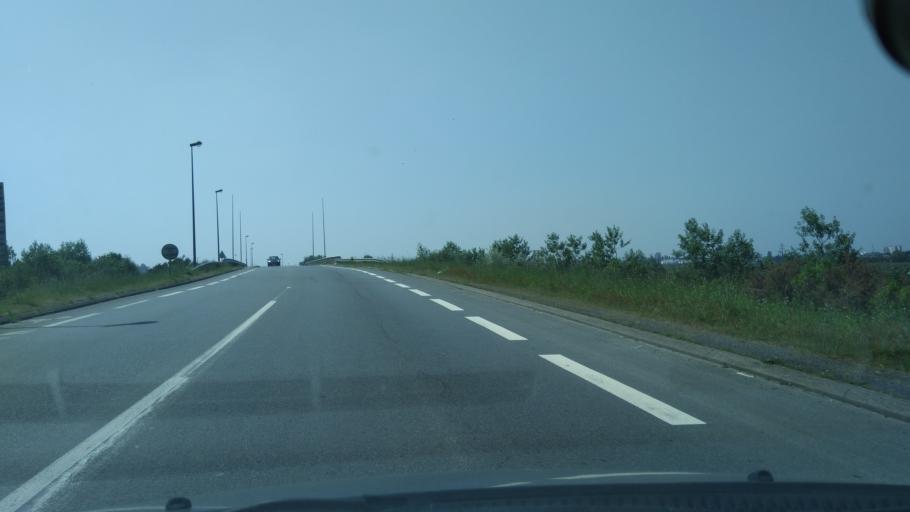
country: FR
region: Pays de la Loire
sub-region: Departement de la Loire-Atlantique
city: Montoir-de-Bretagne
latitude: 47.3255
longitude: -2.1635
